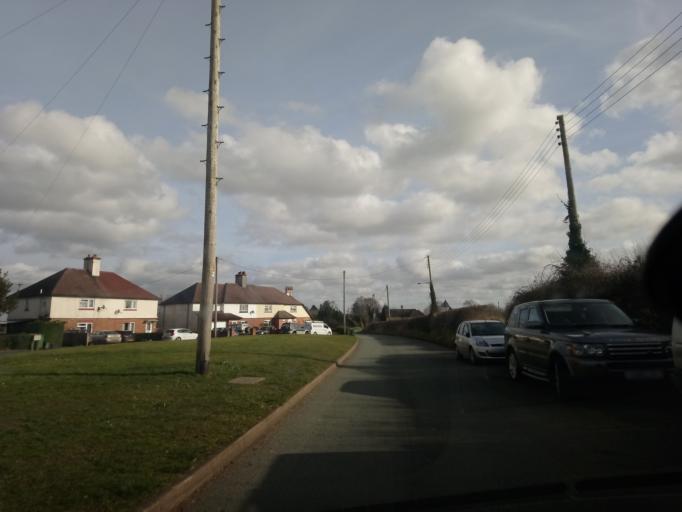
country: GB
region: England
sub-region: Shropshire
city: Stoke upon Tern
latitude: 52.8499
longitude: -2.5670
